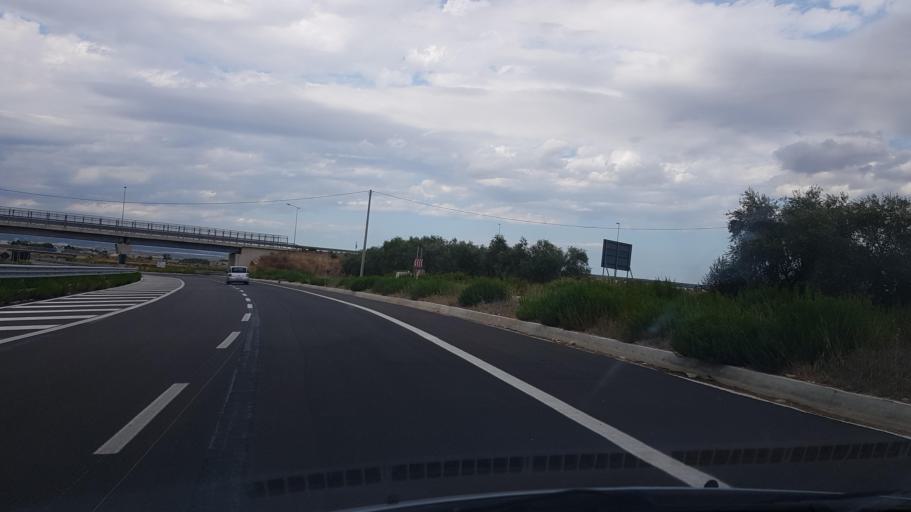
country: IT
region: Apulia
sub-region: Provincia di Taranto
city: Taranto
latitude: 40.4497
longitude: 17.2847
